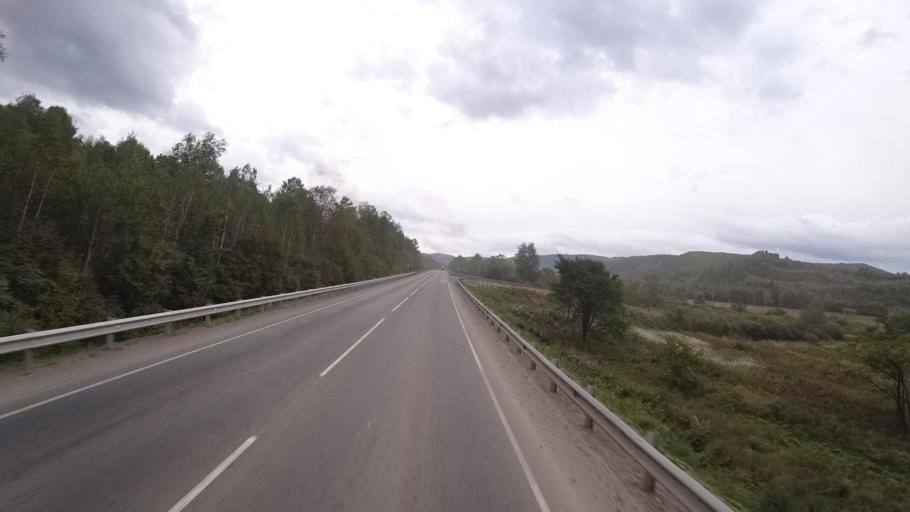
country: RU
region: Jewish Autonomous Oblast
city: Khingansk
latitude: 48.9905
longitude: 131.1213
